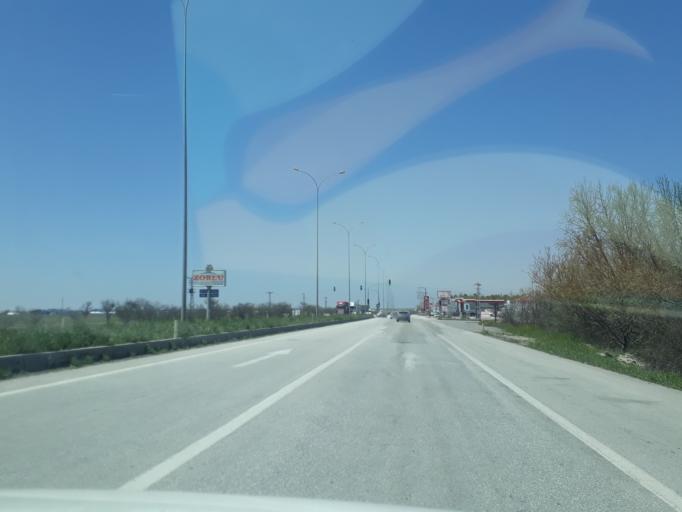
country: TR
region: Konya
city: Karapinar
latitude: 37.7147
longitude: 33.5169
